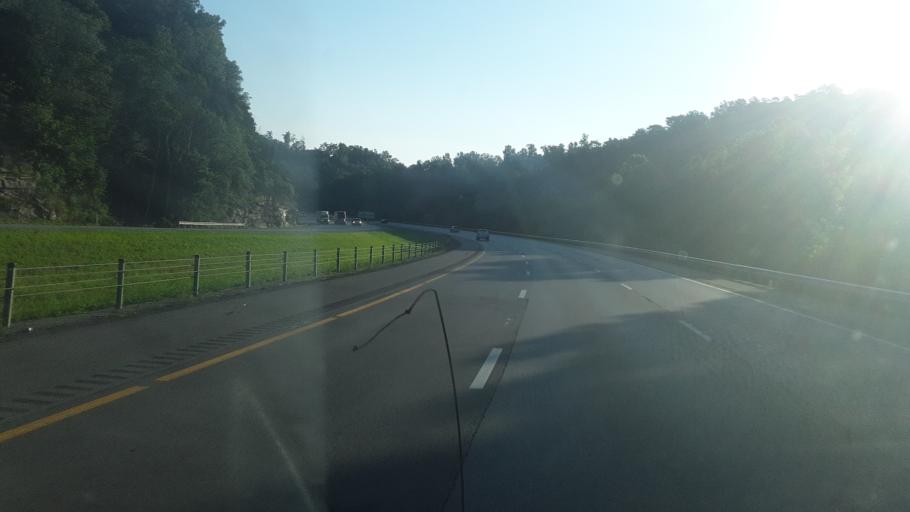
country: US
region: Kentucky
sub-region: Hardin County
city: Elizabethtown
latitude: 37.7414
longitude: -85.7962
